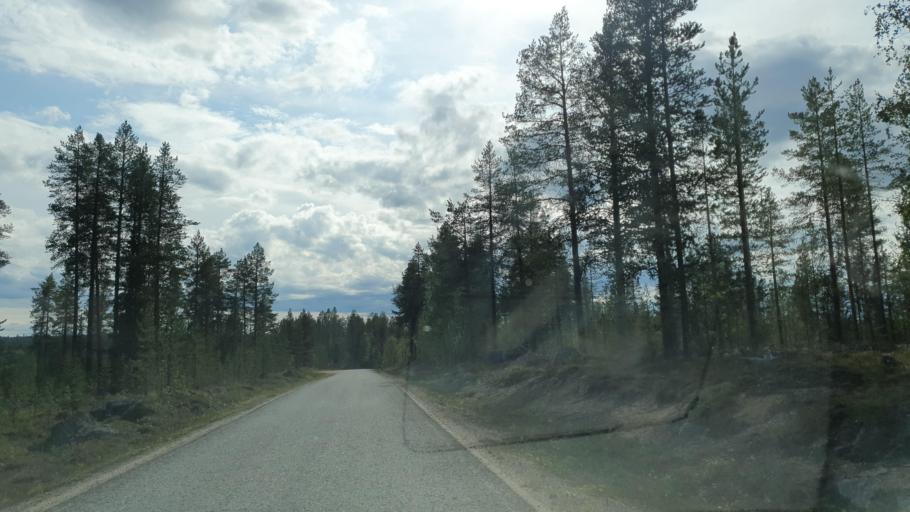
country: FI
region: Lapland
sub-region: Tunturi-Lappi
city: Muonio
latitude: 67.6926
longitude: 24.1100
